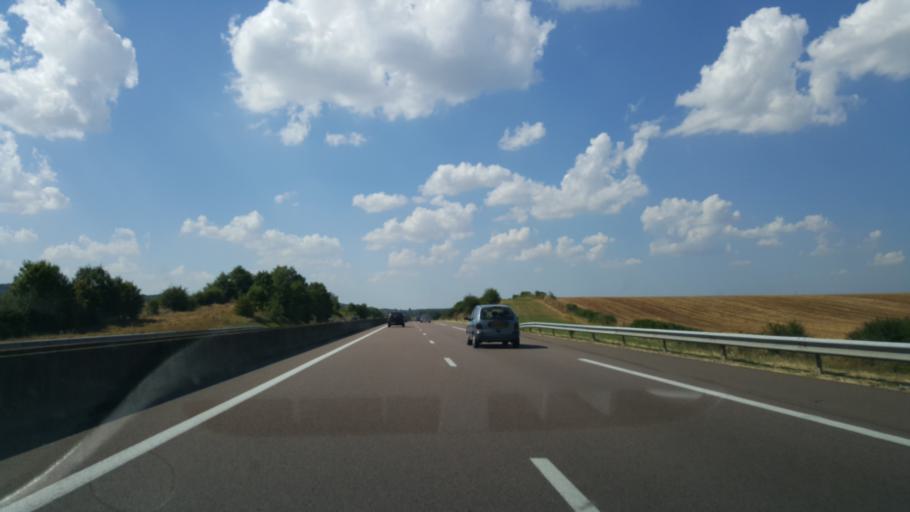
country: FR
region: Bourgogne
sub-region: Departement de la Cote-d'Or
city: Semur-en-Auxois
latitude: 47.3765
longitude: 4.3866
